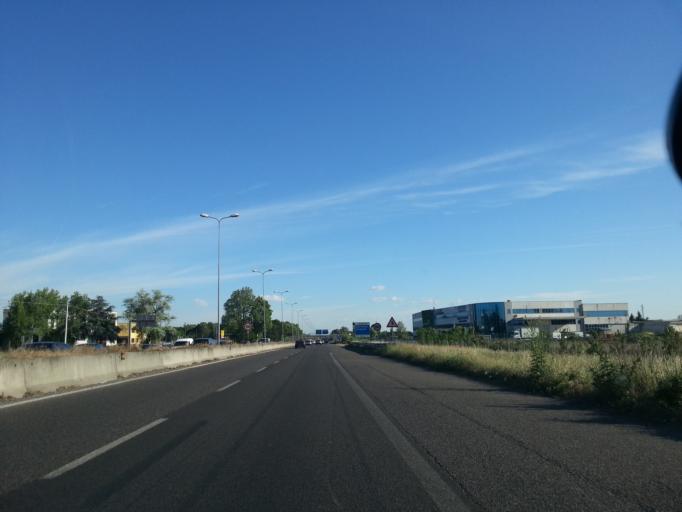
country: IT
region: Lombardy
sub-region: Provincia di Monza e Brianza
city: Varedo
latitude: 45.5840
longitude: 9.1748
